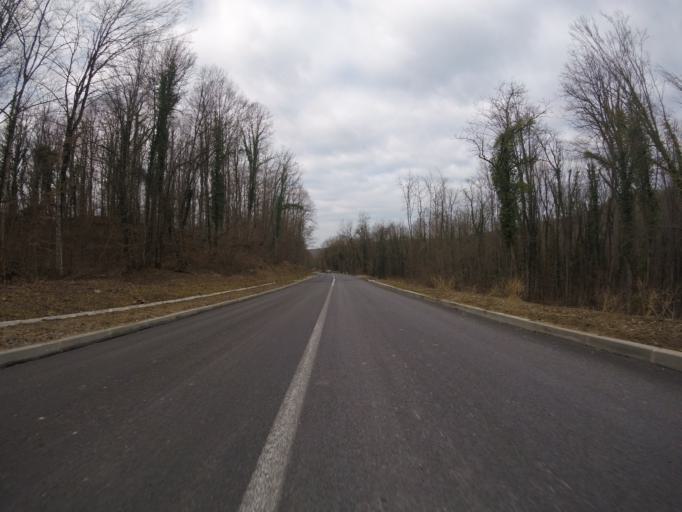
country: HR
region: Sisacko-Moslavacka
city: Glina
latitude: 45.4859
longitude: 16.0436
